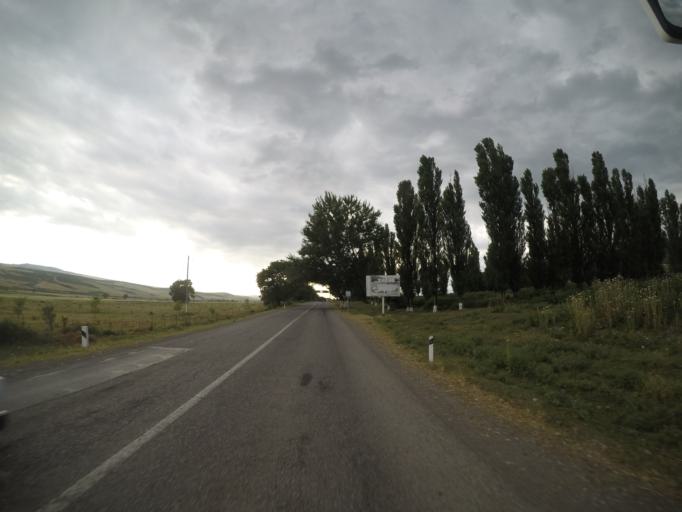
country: AZ
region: Ismayilli
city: Ismayilli
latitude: 40.7560
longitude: 48.2244
